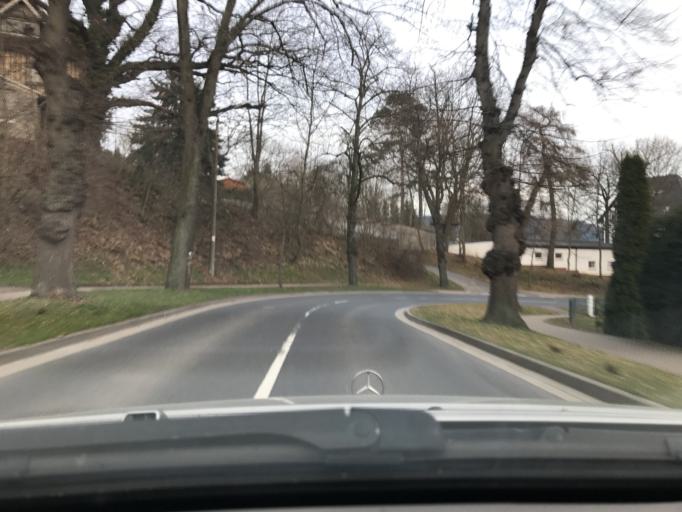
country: DE
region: Thuringia
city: Heilbad Heiligenstadt
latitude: 51.3838
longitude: 10.1314
